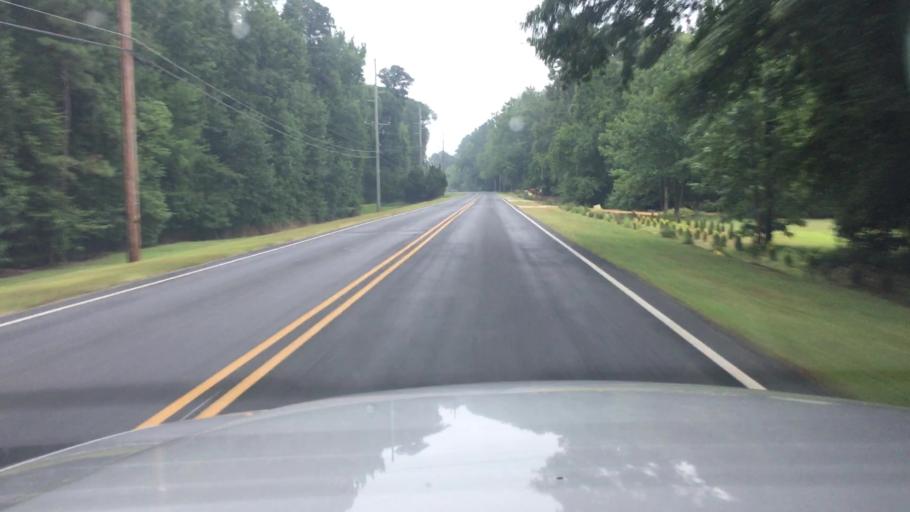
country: US
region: North Carolina
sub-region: Cumberland County
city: Fayetteville
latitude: 35.0032
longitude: -78.8601
